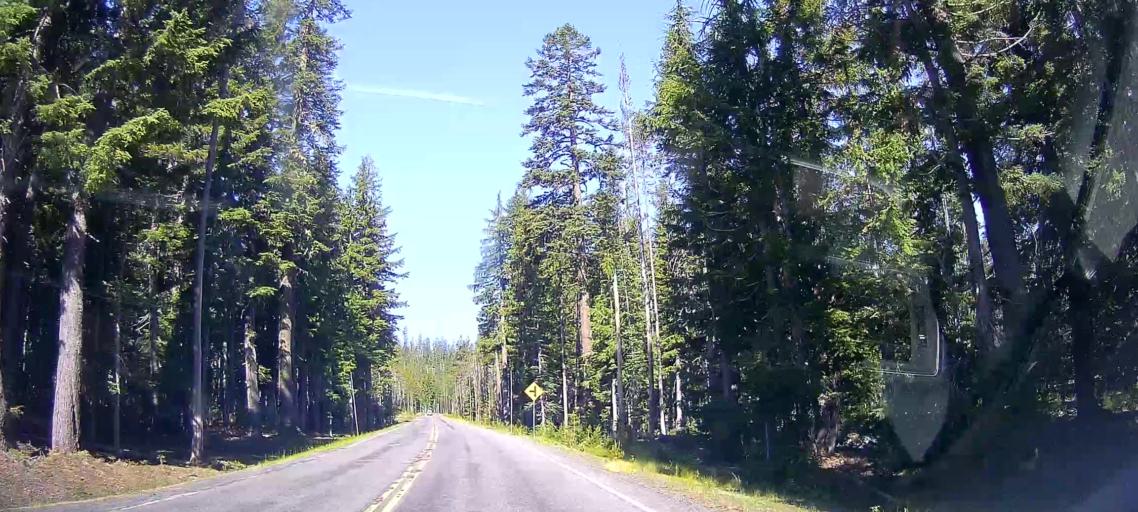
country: US
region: Oregon
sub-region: Jackson County
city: Shady Cove
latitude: 42.8603
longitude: -122.1587
